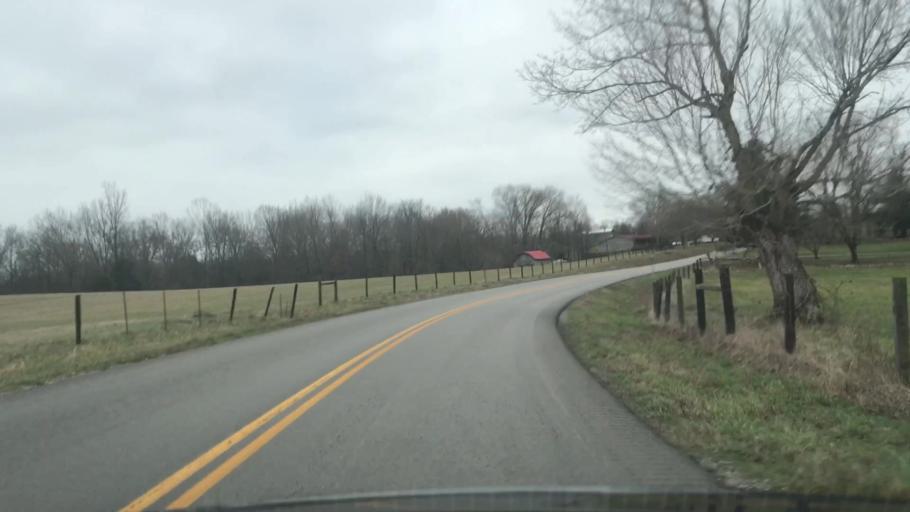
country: US
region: Kentucky
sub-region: Barren County
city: Glasgow
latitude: 36.9108
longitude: -85.7992
